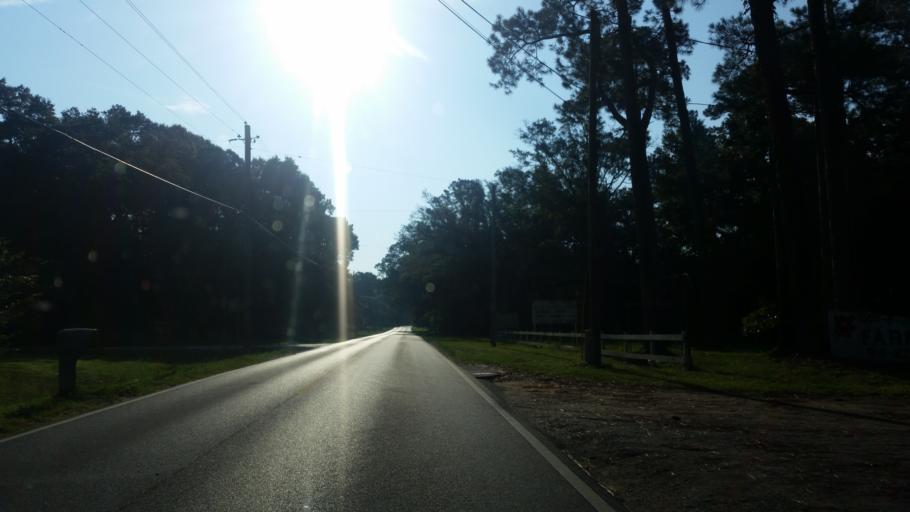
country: US
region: Florida
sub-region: Escambia County
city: Ensley
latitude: 30.5199
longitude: -87.3249
